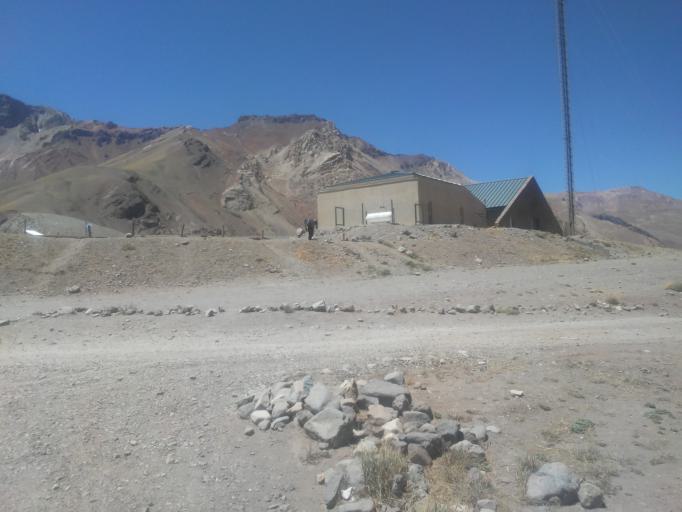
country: CL
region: Valparaiso
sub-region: Provincia de Los Andes
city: Los Andes
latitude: -32.8241
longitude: -69.9427
